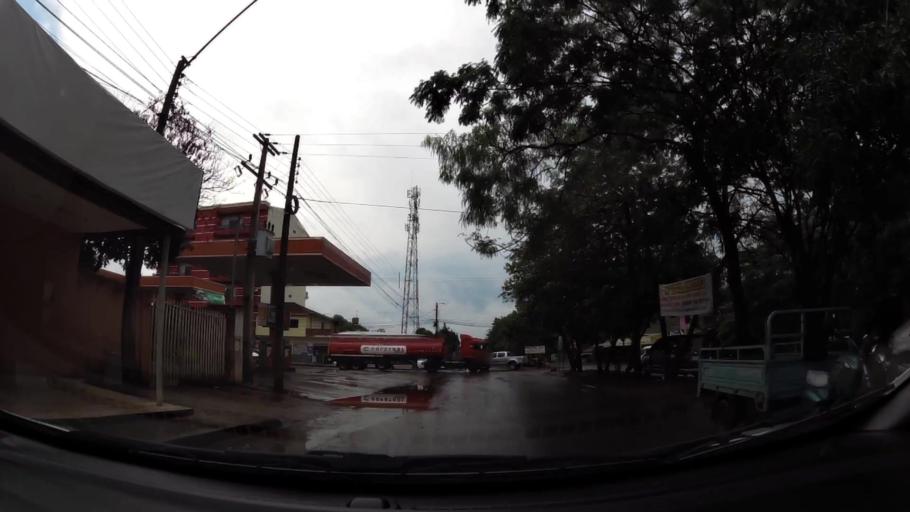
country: PY
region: Alto Parana
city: Presidente Franco
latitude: -25.5209
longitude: -54.6644
